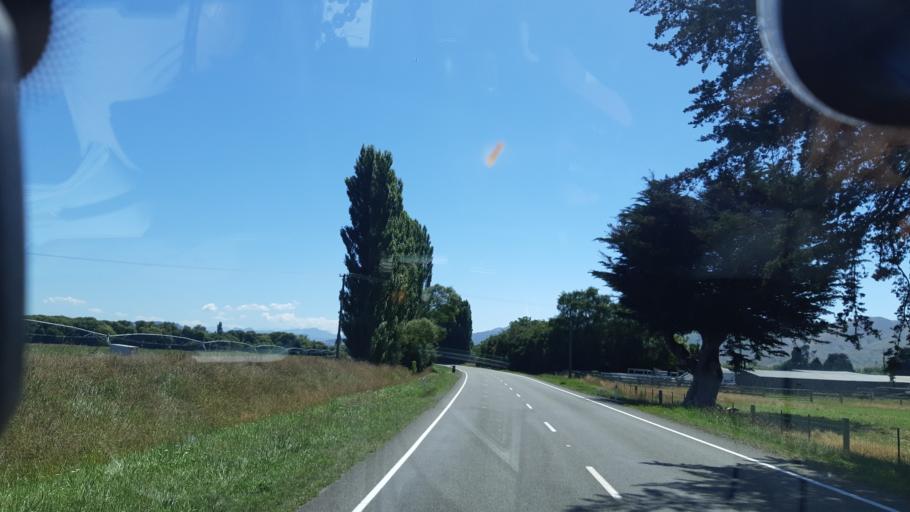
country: NZ
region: Canterbury
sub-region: Kaikoura District
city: Kaikoura
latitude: -42.7356
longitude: 173.2713
